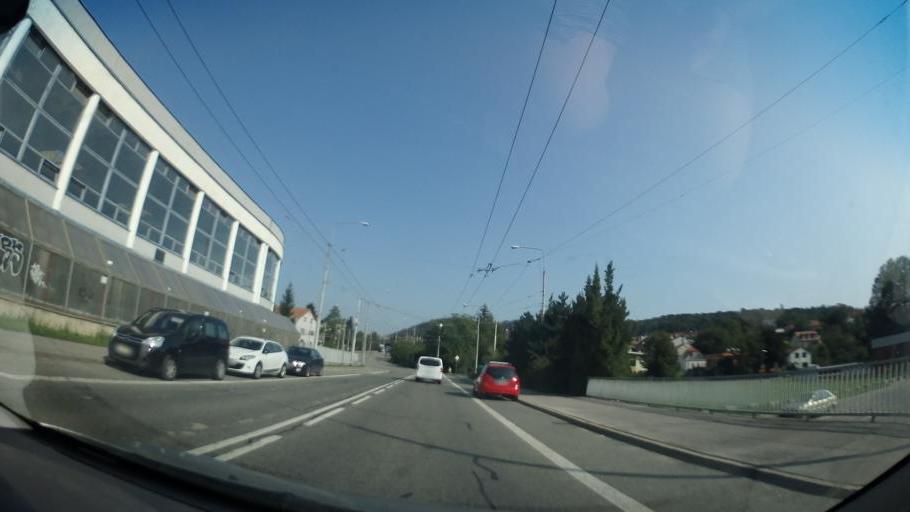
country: CZ
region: South Moravian
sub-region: Mesto Brno
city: Brno
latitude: 49.2151
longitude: 16.5600
